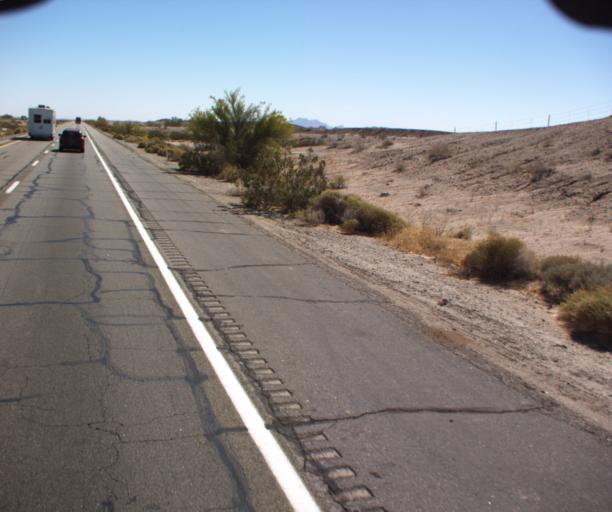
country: US
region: Arizona
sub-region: Yuma County
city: Wellton
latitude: 32.6558
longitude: -114.2385
